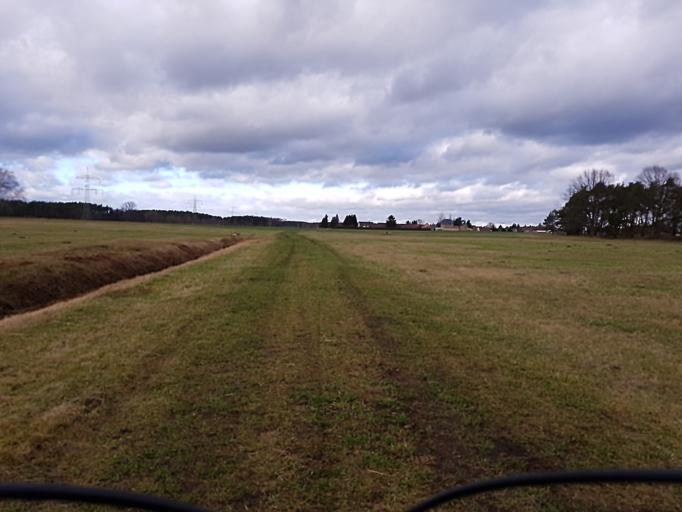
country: DE
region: Brandenburg
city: Schilda
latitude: 51.5814
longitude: 13.3843
